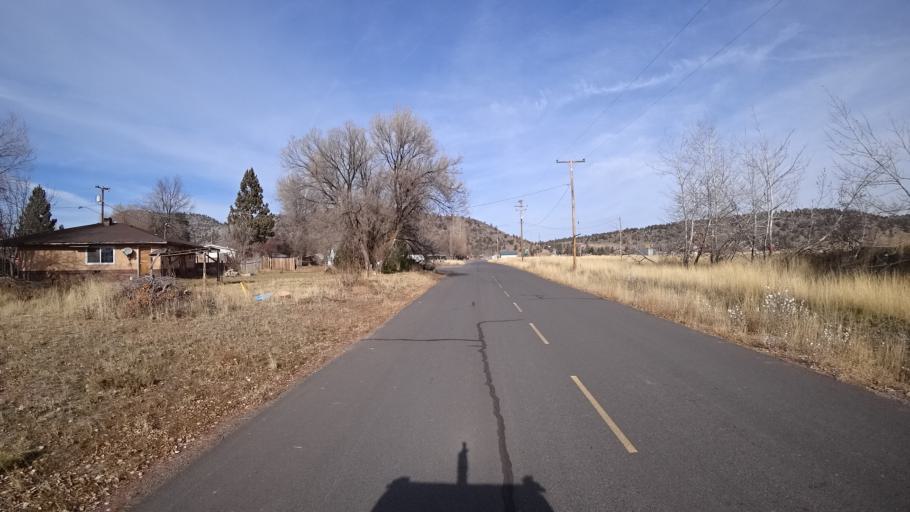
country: US
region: Oregon
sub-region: Klamath County
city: Klamath Falls
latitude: 41.9653
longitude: -121.9166
